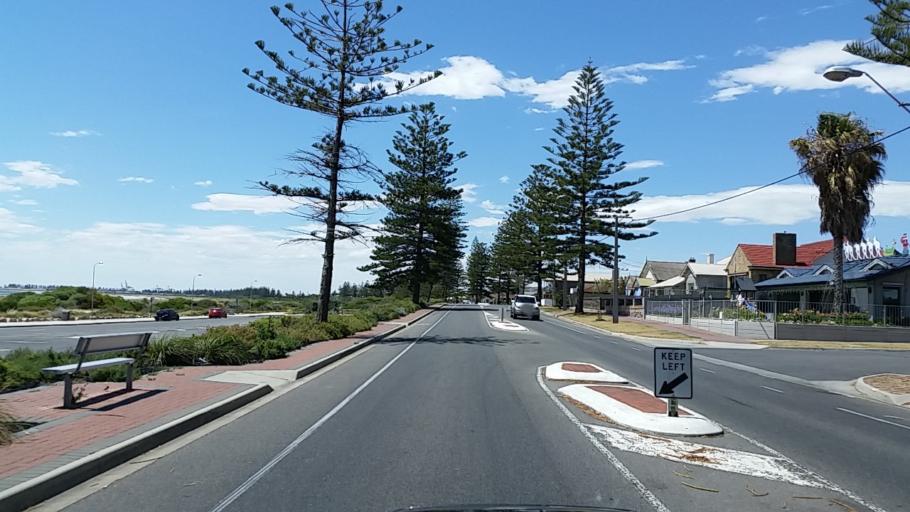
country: AU
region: South Australia
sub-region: Port Adelaide Enfield
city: Birkenhead
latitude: -34.8231
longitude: 138.4878
